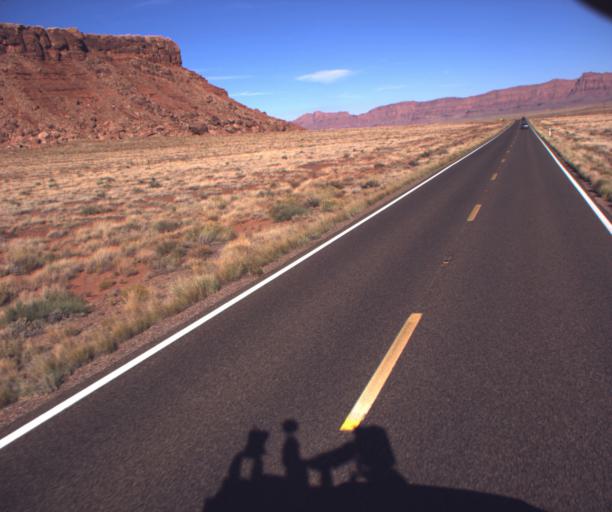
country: US
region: Arizona
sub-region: Coconino County
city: Page
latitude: 36.7516
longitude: -111.7257
